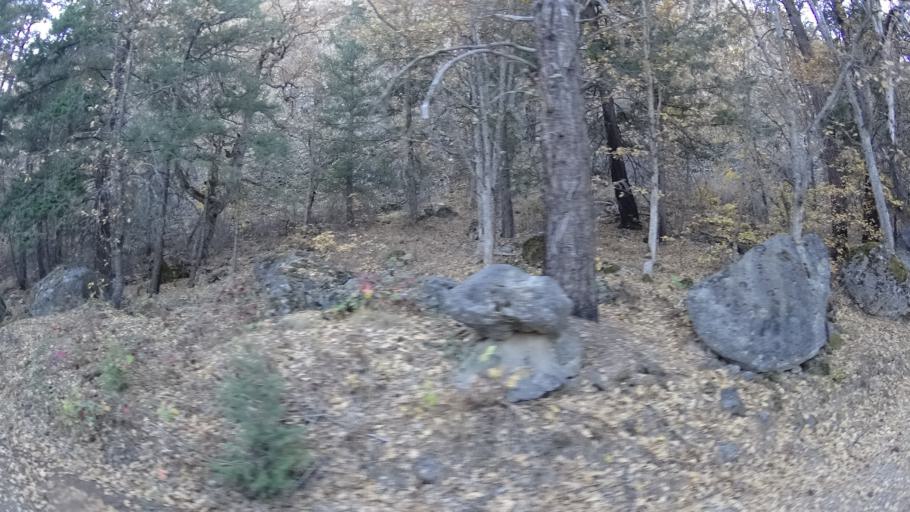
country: US
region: California
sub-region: Siskiyou County
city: Yreka
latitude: 41.8467
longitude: -122.6888
